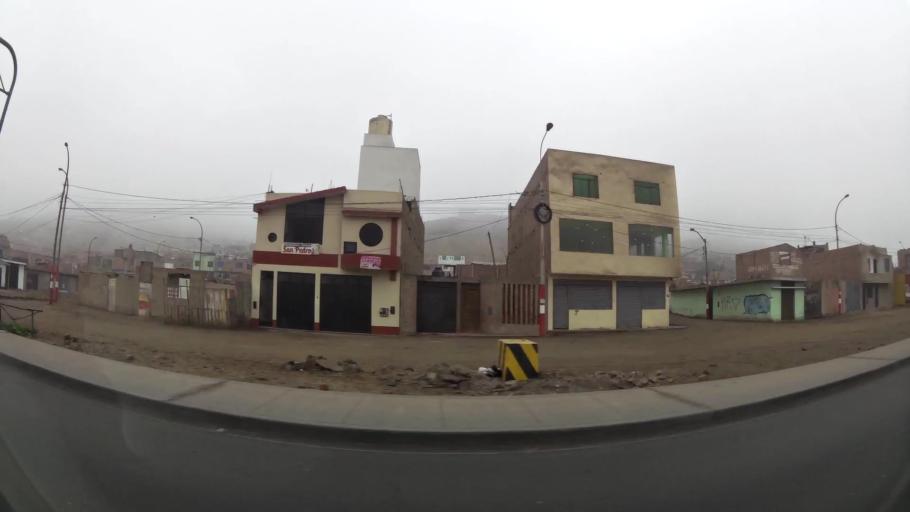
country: PE
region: Lima
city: Ventanilla
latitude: -11.8443
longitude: -77.1175
